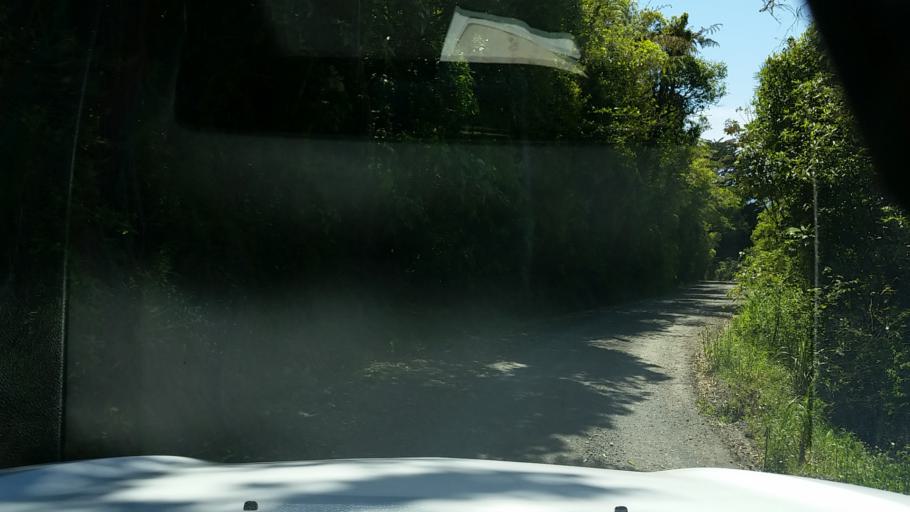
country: NZ
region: Auckland
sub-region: Auckland
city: Titirangi
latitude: -36.9271
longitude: 174.5819
